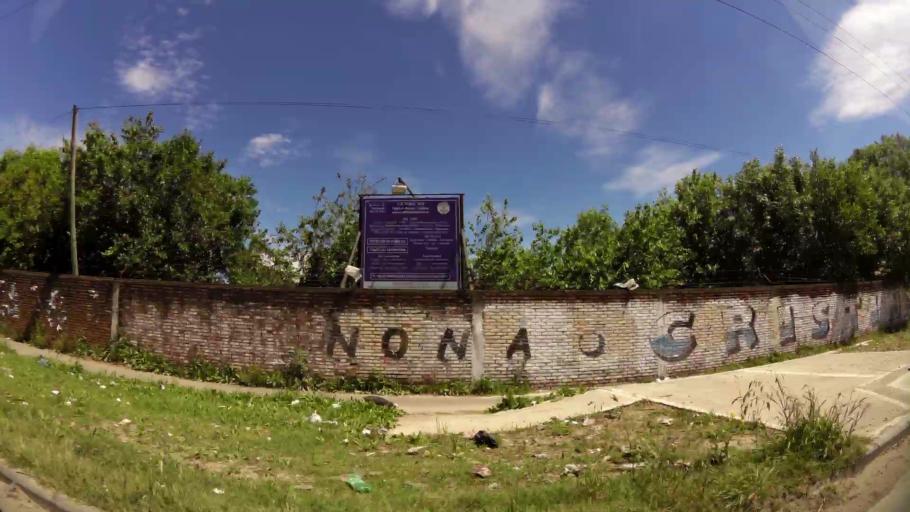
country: AR
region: Buenos Aires
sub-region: Partido de Lanus
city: Lanus
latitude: -34.7297
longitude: -58.3297
